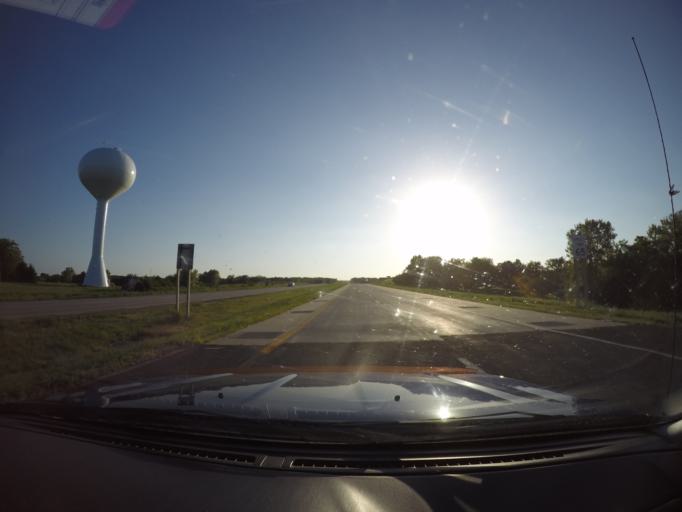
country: US
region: Kansas
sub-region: Pottawatomie County
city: Wamego
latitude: 39.2104
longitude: -96.3285
